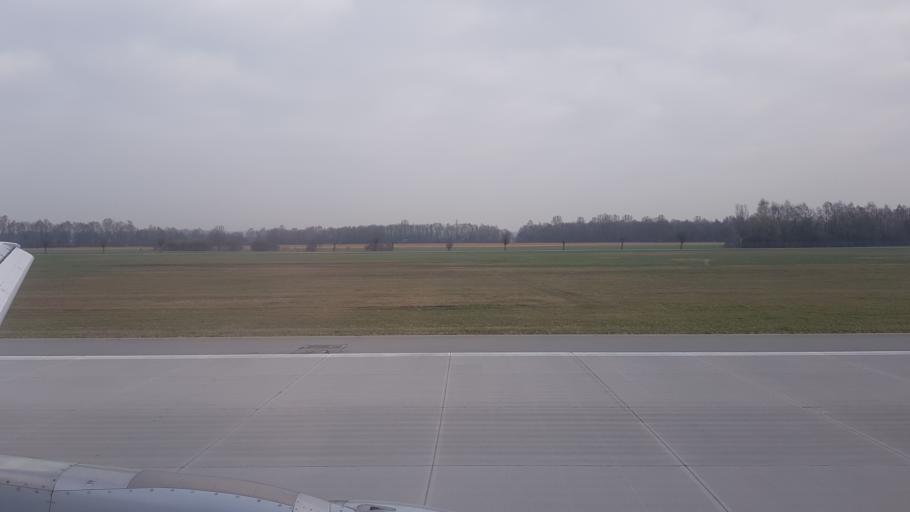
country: DE
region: Bavaria
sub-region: Upper Bavaria
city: Marzling
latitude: 48.3644
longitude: 11.7884
